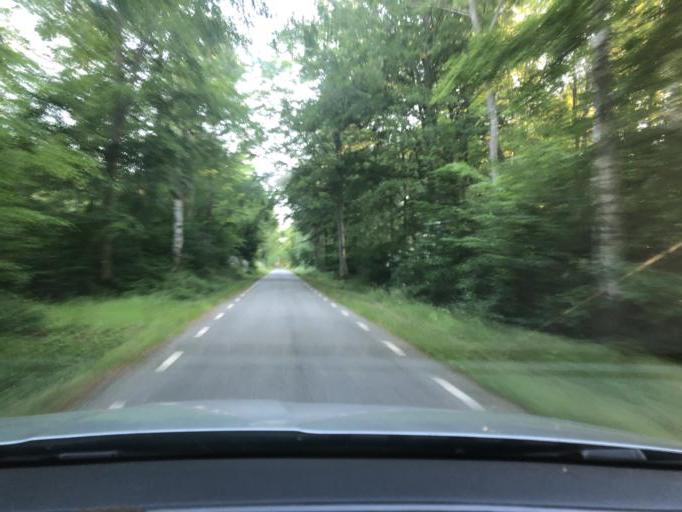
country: SE
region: Blekinge
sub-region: Solvesborgs Kommun
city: Soelvesborg
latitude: 56.1384
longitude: 14.6249
